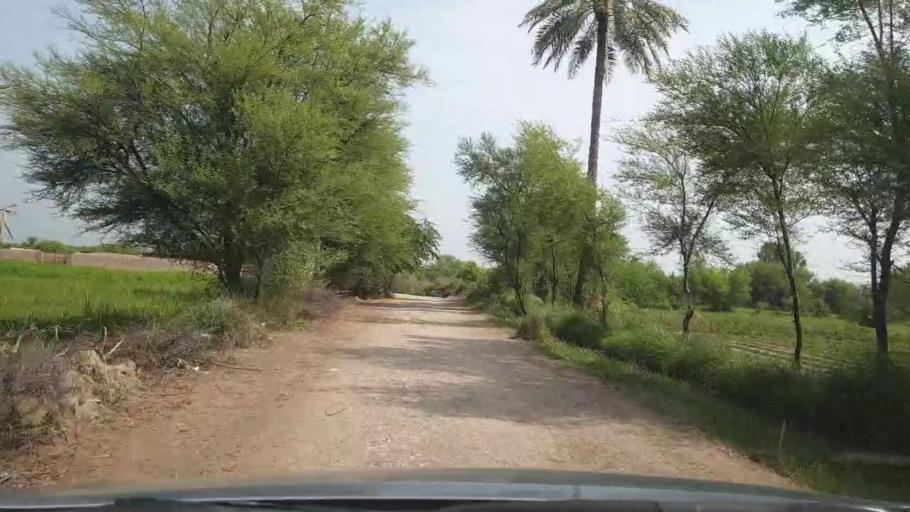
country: PK
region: Sindh
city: Rohri
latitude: 27.6493
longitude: 69.0233
